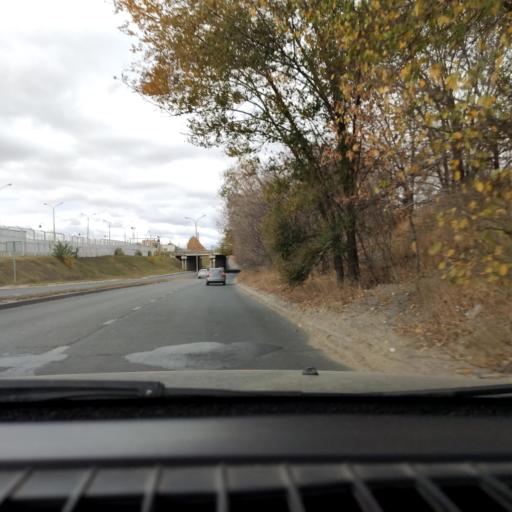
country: RU
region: Samara
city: Tol'yatti
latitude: 53.5668
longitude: 49.2874
